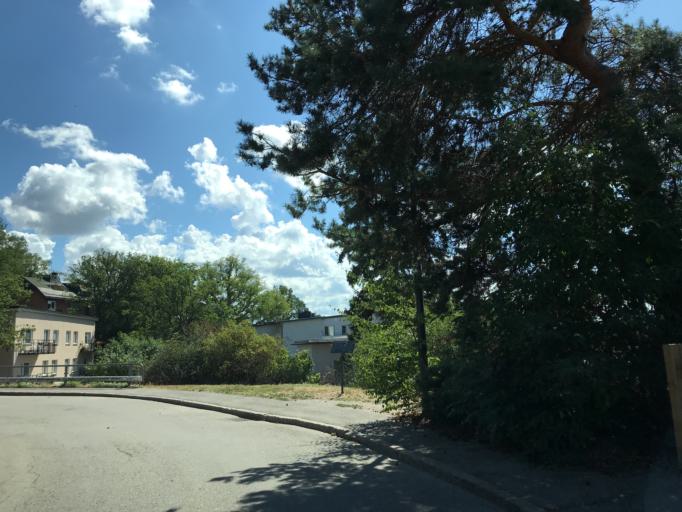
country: SE
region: Stockholm
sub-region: Sundbybergs Kommun
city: Sundbyberg
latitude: 59.3192
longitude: 17.9808
